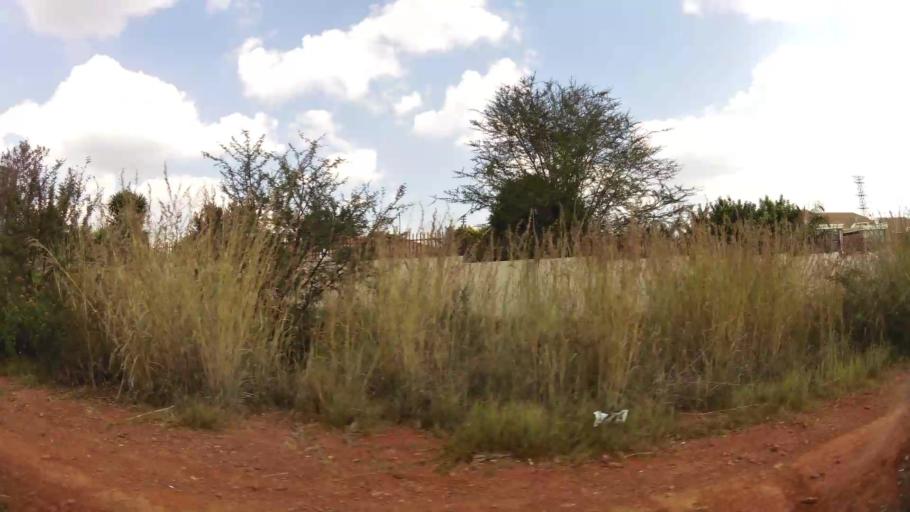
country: ZA
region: Gauteng
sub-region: City of Tshwane Metropolitan Municipality
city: Centurion
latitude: -25.8103
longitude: 28.3313
